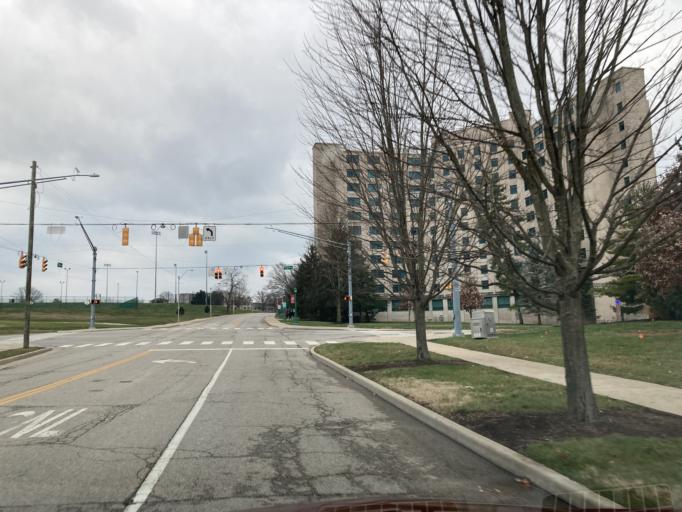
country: US
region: Indiana
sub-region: Monroe County
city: Bloomington
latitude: 39.1795
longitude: -86.5191
